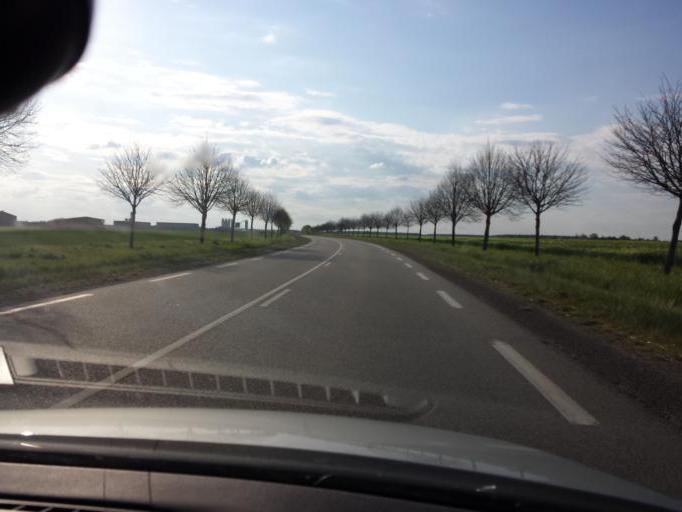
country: FR
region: Haute-Normandie
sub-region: Departement de l'Eure
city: Breteuil
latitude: 48.8423
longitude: 0.9324
